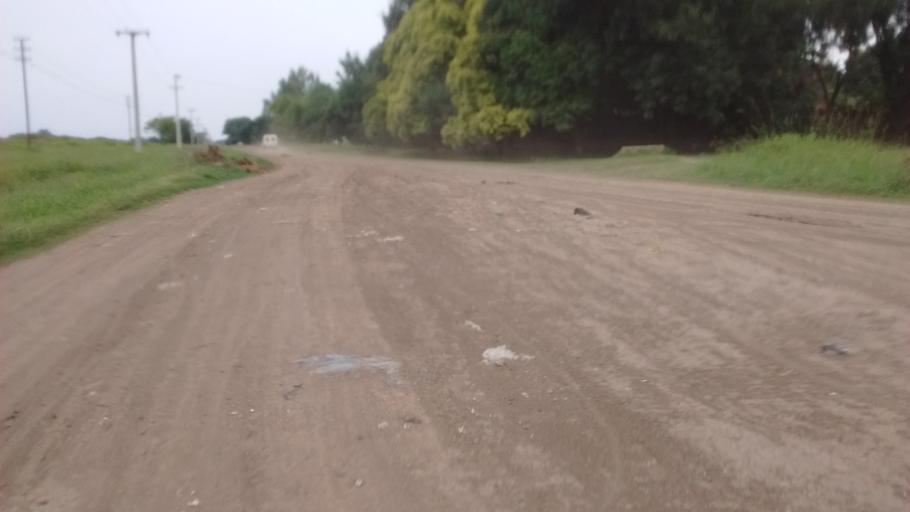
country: AR
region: Santa Fe
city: Funes
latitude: -32.9126
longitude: -60.8365
